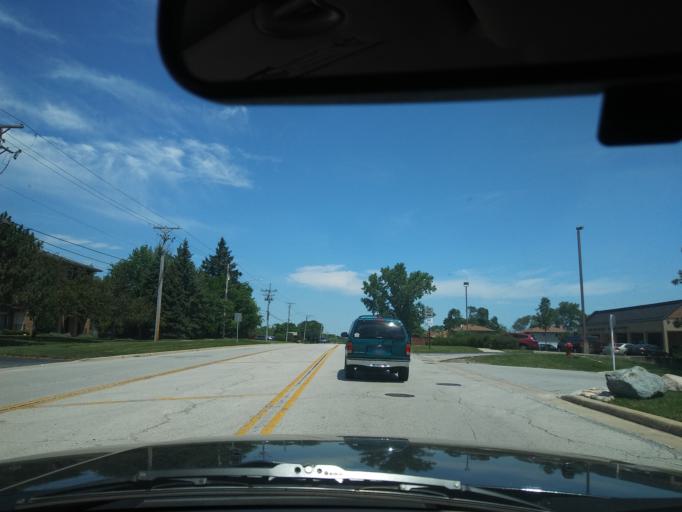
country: US
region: Illinois
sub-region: Cook County
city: Oak Forest
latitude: 41.6047
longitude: -87.7560
